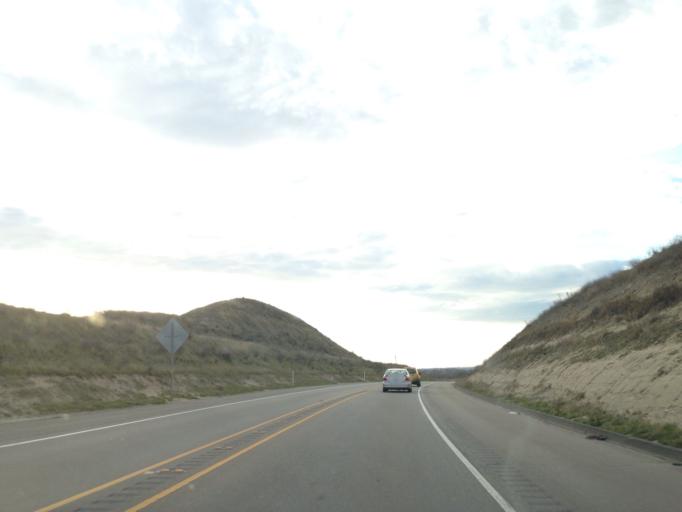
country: US
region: California
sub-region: San Luis Obispo County
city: Shandon
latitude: 35.6626
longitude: -120.3645
